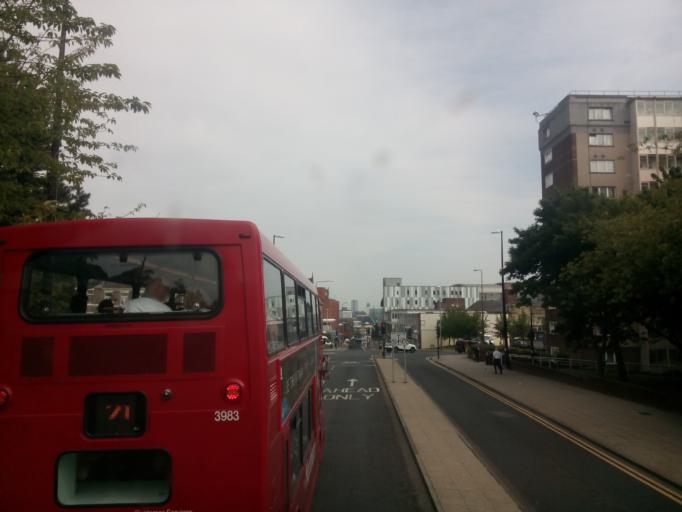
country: GB
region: England
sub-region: Gateshead
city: Gateshead
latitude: 54.9600
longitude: -1.6025
